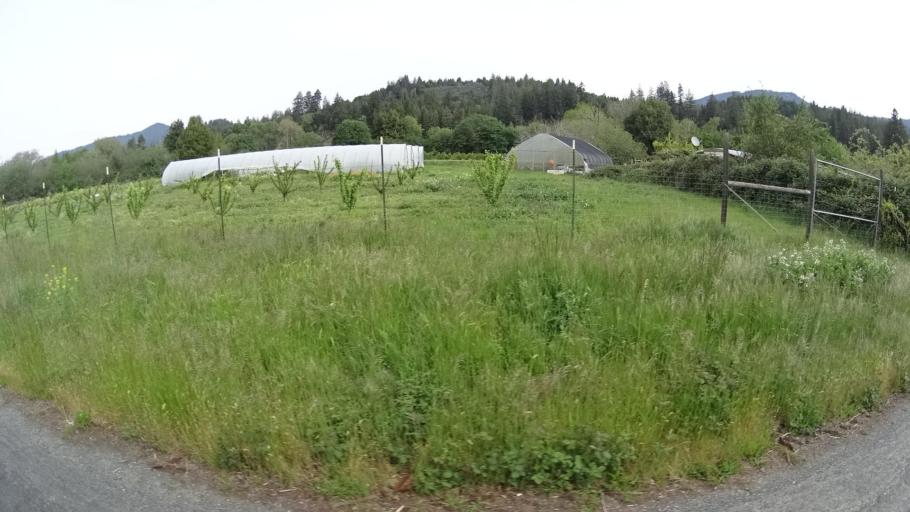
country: US
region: California
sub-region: Humboldt County
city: Redway
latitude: 40.3432
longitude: -123.8896
